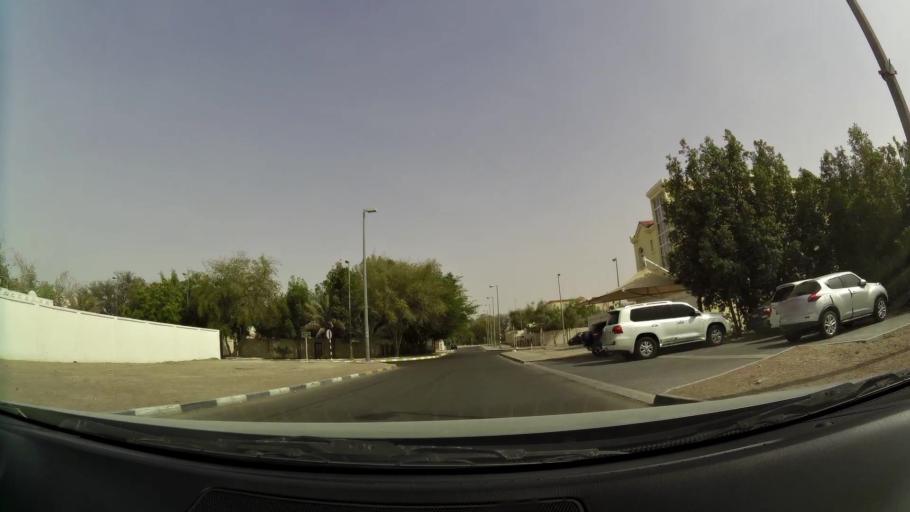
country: AE
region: Abu Dhabi
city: Al Ain
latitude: 24.1876
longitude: 55.6339
